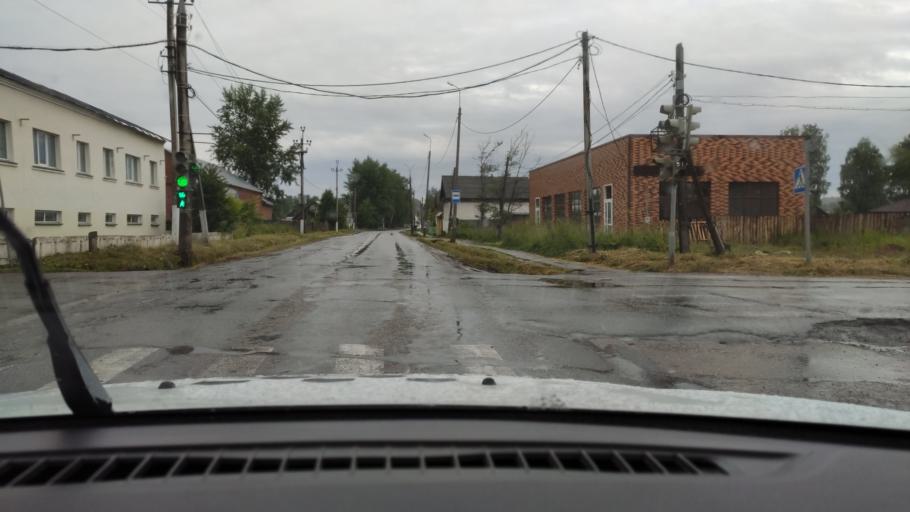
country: RU
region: Udmurtiya
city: Votkinsk
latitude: 57.0490
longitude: 53.9652
